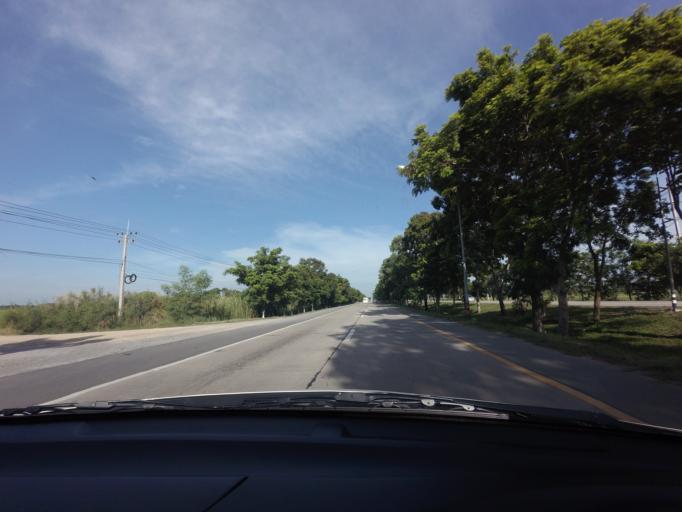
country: TH
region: Suphan Buri
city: Bang Pla Ma
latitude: 14.3375
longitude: 100.1991
